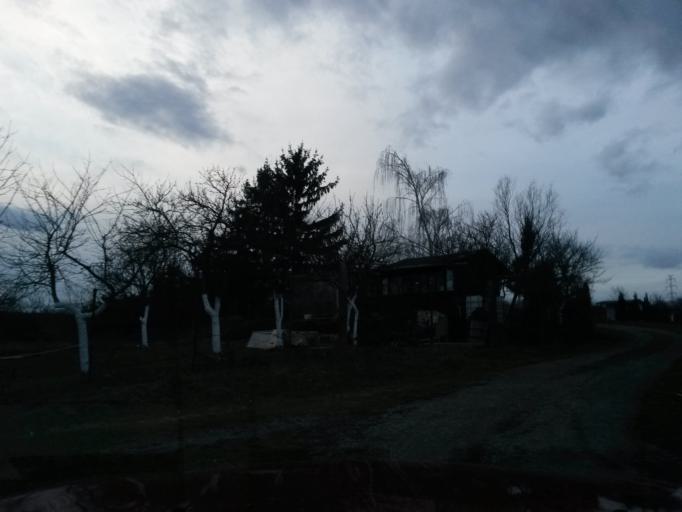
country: SK
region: Kosicky
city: Kosice
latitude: 48.7260
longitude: 21.3083
